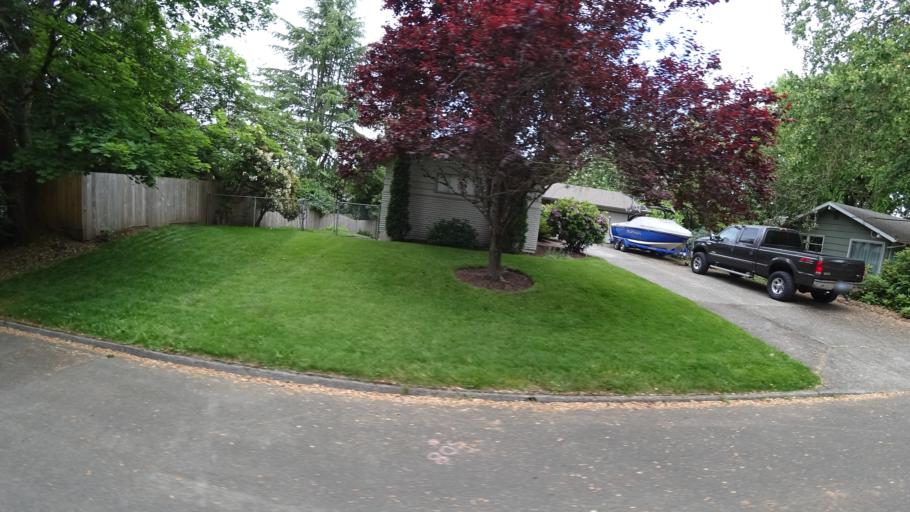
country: US
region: Oregon
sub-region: Clackamas County
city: Lake Oswego
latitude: 45.4634
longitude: -122.6866
